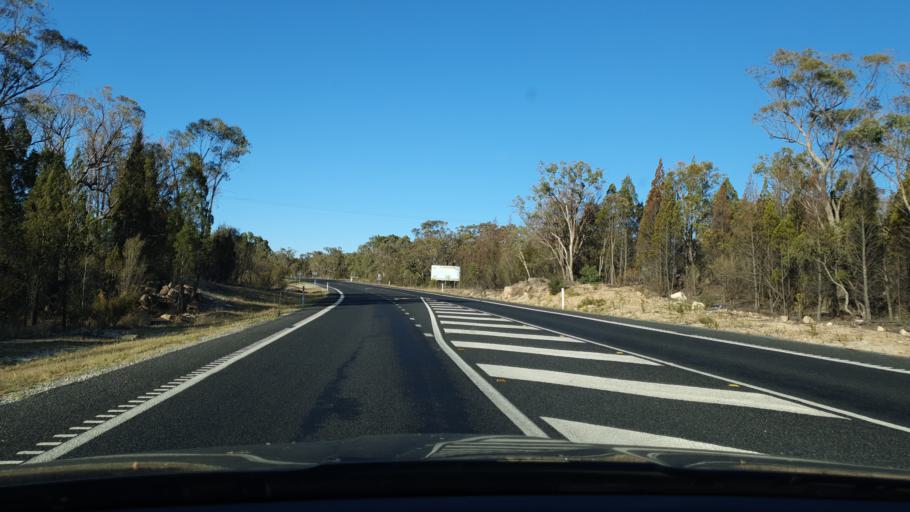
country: AU
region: Queensland
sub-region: Southern Downs
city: Stanthorpe
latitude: -28.6822
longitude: 151.9189
